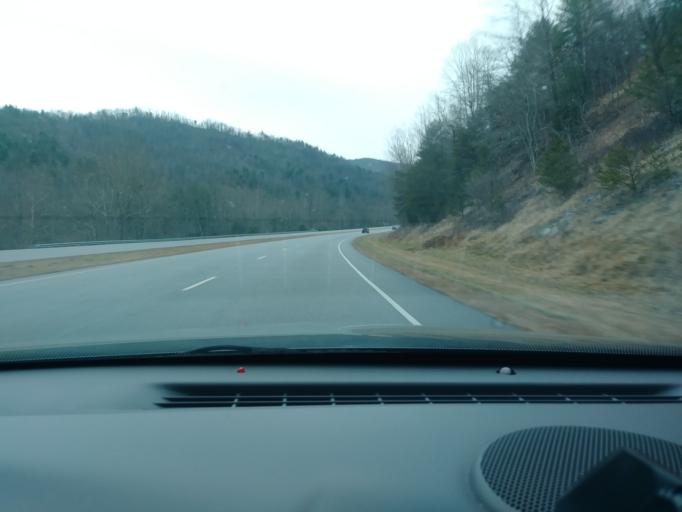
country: US
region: North Carolina
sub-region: Wilkes County
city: Millers Creek
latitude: 36.1810
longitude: -81.3930
